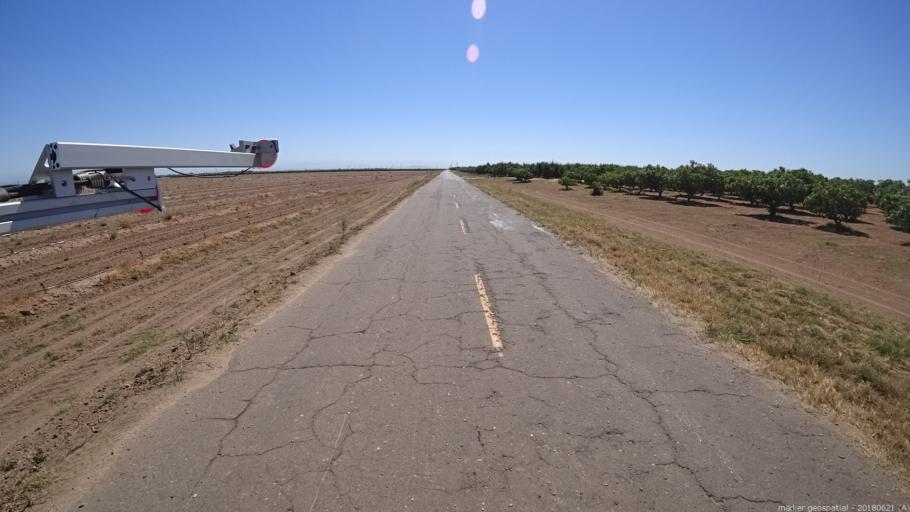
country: US
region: California
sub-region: Madera County
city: Parksdale
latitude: 36.9095
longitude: -119.9445
